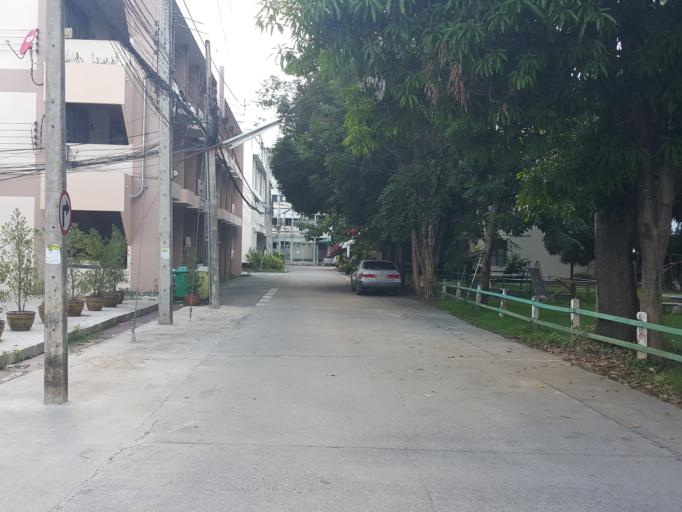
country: TH
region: Lampang
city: Lampang
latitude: 18.2885
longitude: 99.5076
